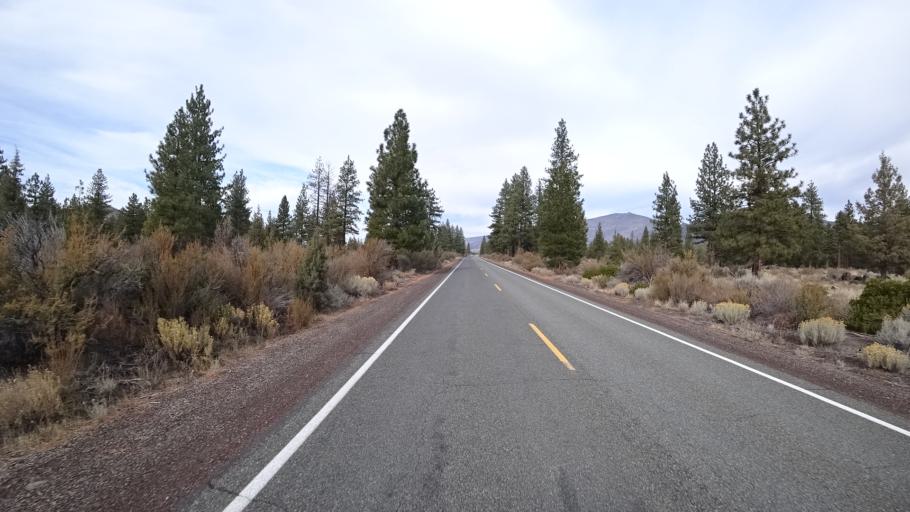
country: US
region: California
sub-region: Siskiyou County
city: Weed
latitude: 41.5432
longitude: -122.2463
